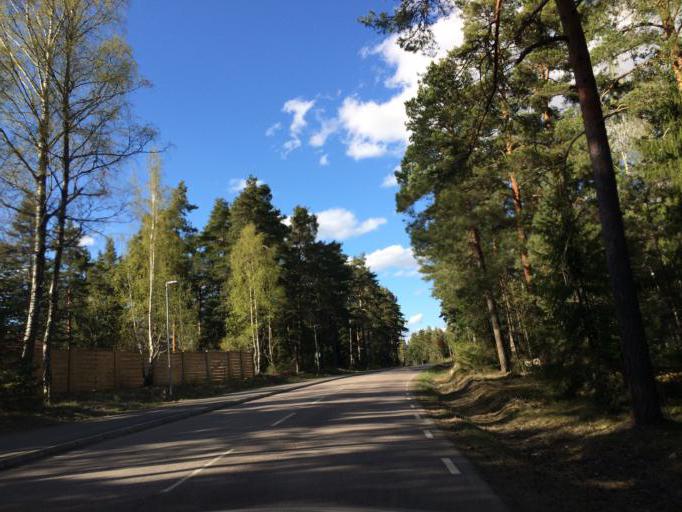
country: SE
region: Soedermanland
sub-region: Eskilstuna Kommun
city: Hallbybrunn
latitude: 59.3509
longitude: 16.4383
